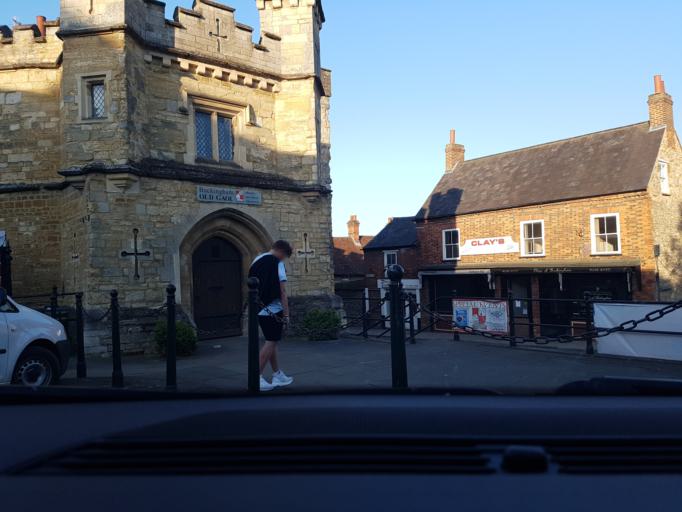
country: GB
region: England
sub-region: Buckinghamshire
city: Buckingham
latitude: 52.0009
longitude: -0.9866
